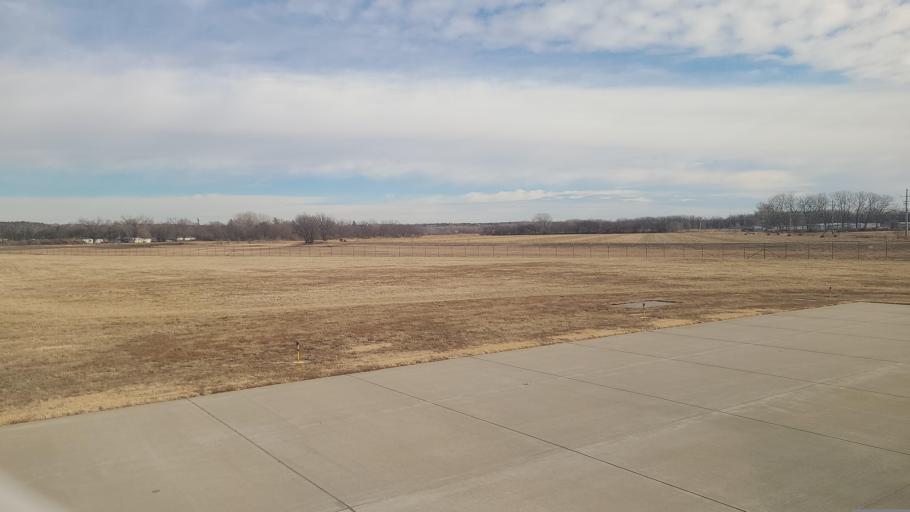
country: US
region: Kansas
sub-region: Riley County
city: Ogden
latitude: 39.1464
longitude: -96.6627
